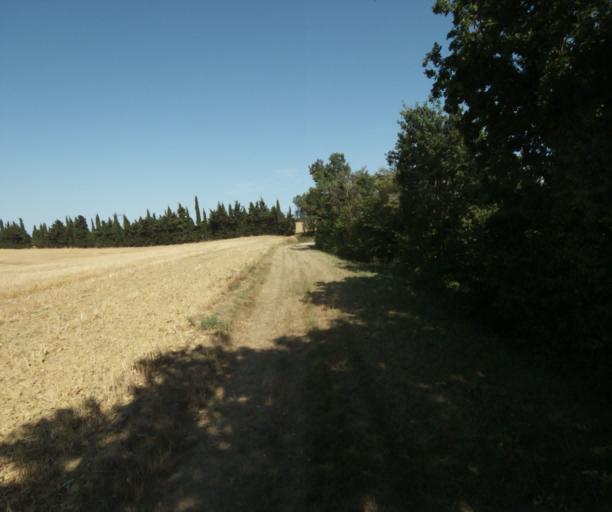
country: FR
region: Midi-Pyrenees
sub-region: Departement de la Haute-Garonne
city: Saint-Felix-Lauragais
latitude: 43.4391
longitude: 1.8502
